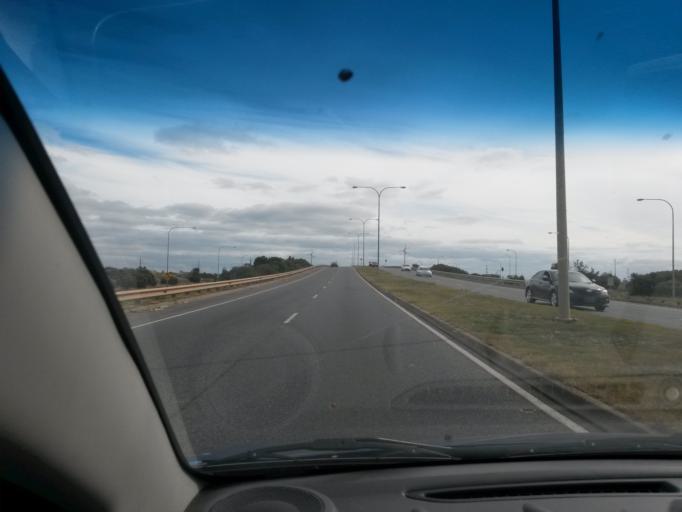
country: AU
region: South Australia
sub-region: Salisbury
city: Ingle Farm
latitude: -34.8094
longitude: 138.5994
